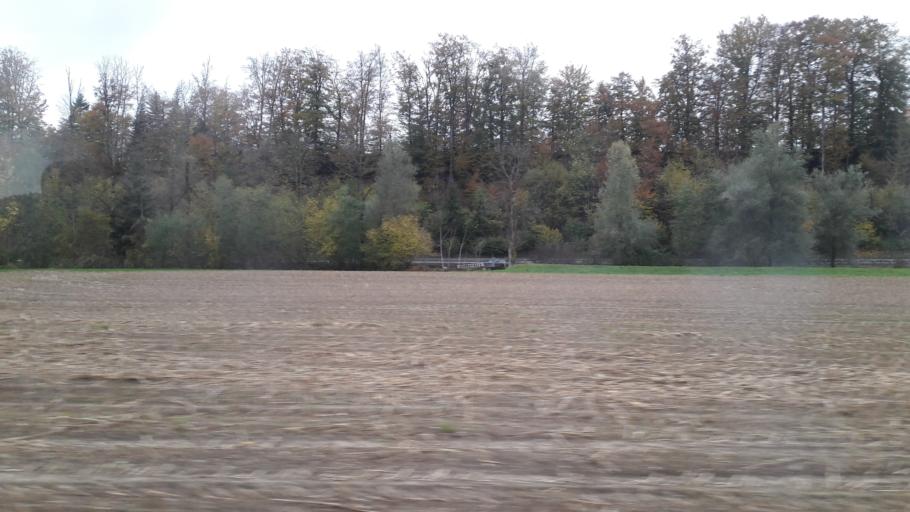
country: CH
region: Bern
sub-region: Emmental District
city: Trachselwald
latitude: 47.0125
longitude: 7.7251
